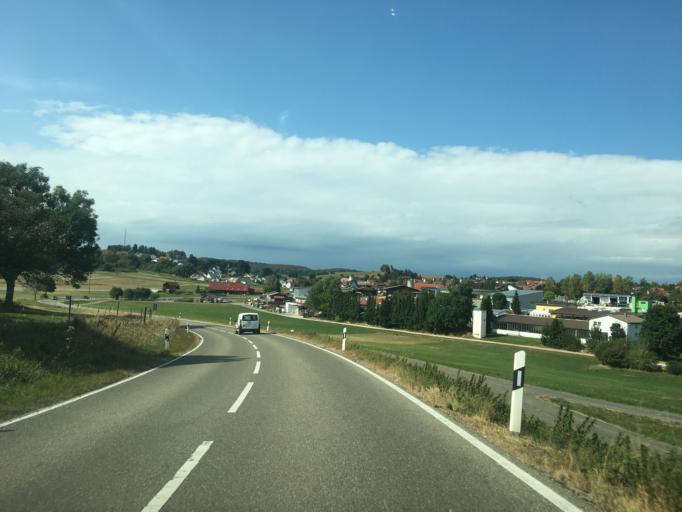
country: DE
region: Baden-Wuerttemberg
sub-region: Tuebingen Region
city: Pfullingen
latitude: 48.3832
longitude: 9.1921
